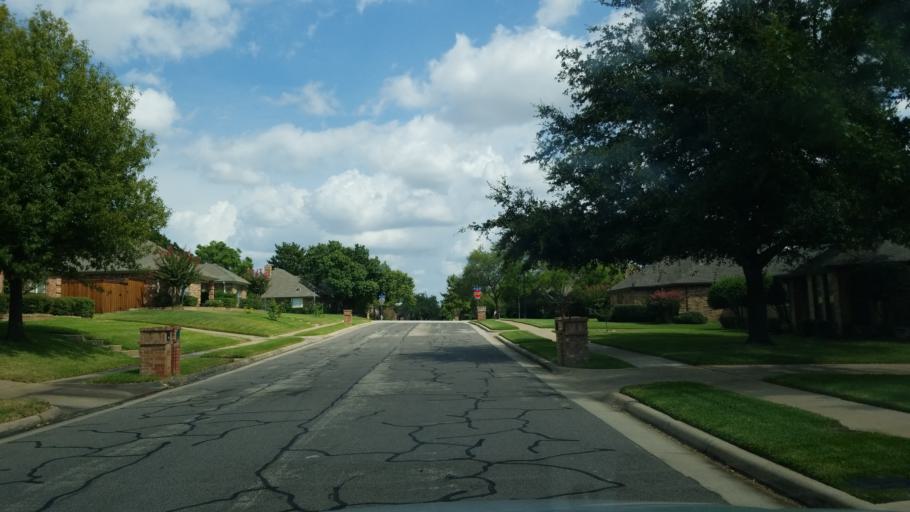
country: US
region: Texas
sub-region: Tarrant County
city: Euless
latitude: 32.8715
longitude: -97.0917
